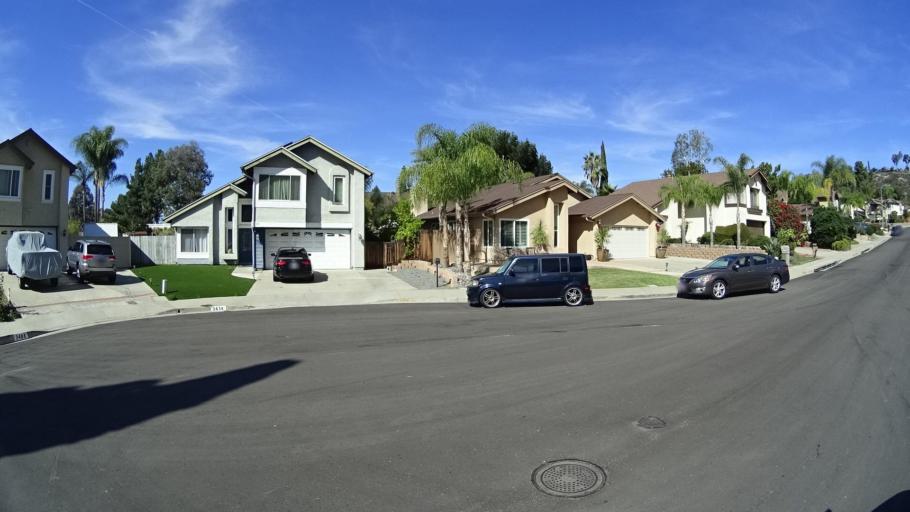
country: US
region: California
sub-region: San Diego County
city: Rancho San Diego
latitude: 32.7451
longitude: -116.9534
